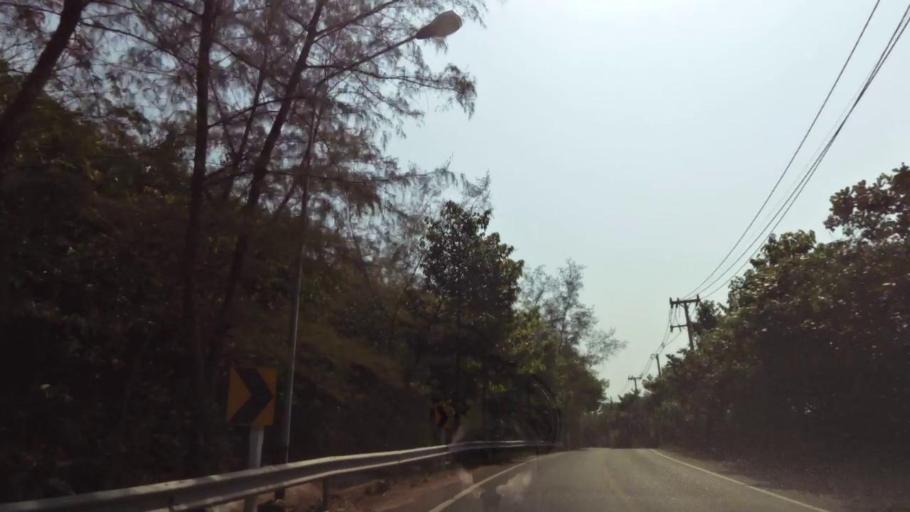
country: TH
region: Chanthaburi
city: Tha Mai
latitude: 12.5313
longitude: 101.9453
